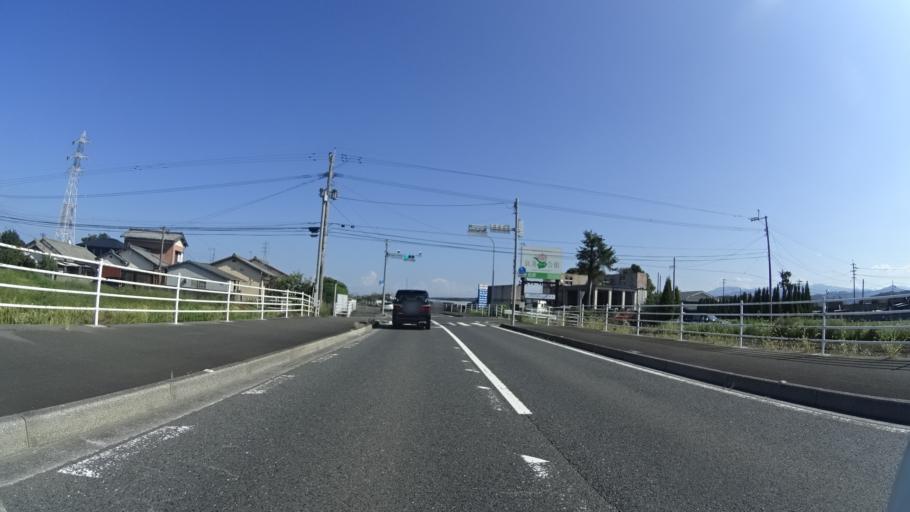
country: JP
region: Fukuoka
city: Tsuiki
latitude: 33.6660
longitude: 131.0268
